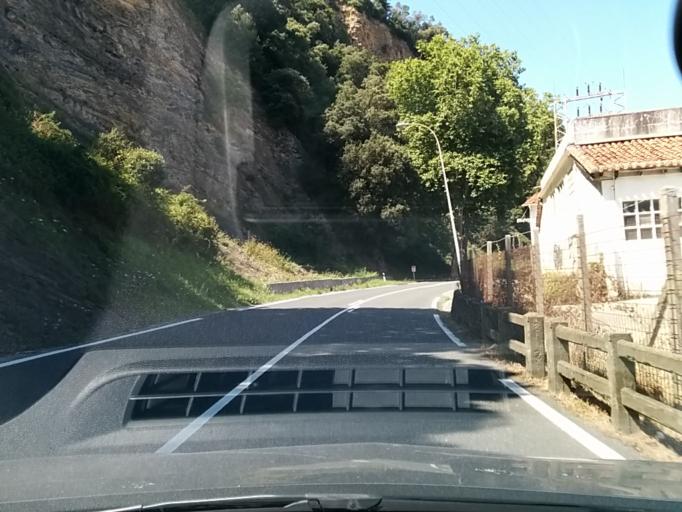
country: ES
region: Basque Country
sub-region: Provincia de Guipuzcoa
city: Deba
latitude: 43.2974
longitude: -2.3573
